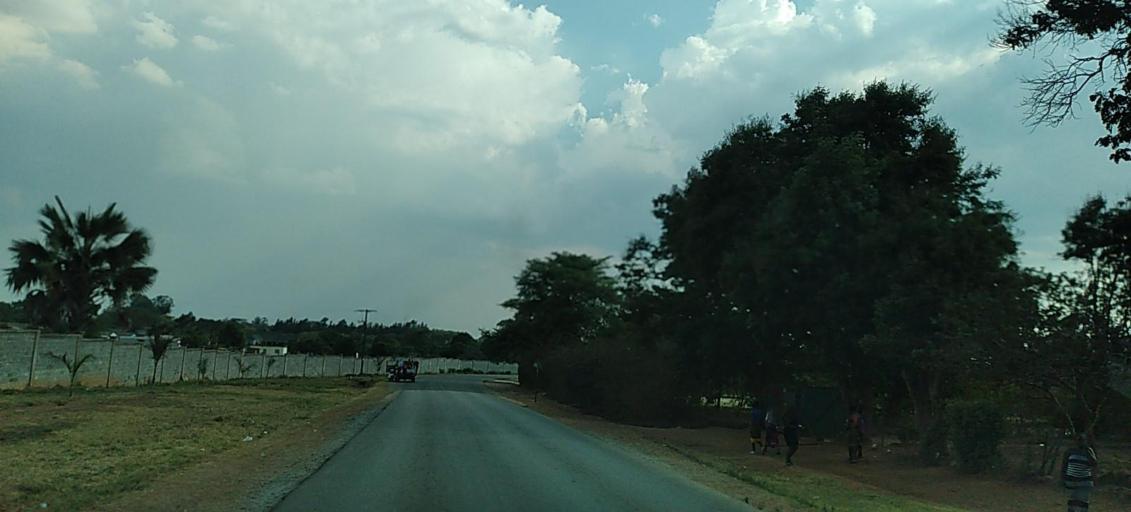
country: ZM
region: Lusaka
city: Lusaka
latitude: -15.5156
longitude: 28.2374
